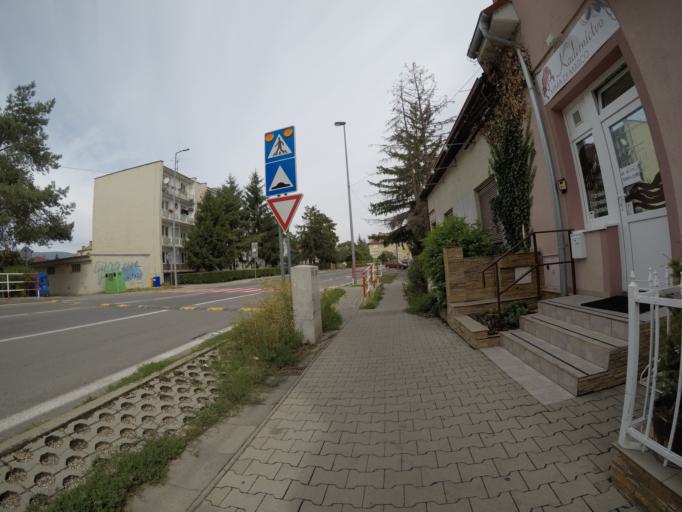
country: SK
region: Trenciansky
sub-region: Okres Nove Mesto nad Vahom
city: Nove Mesto nad Vahom
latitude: 48.7503
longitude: 17.8335
